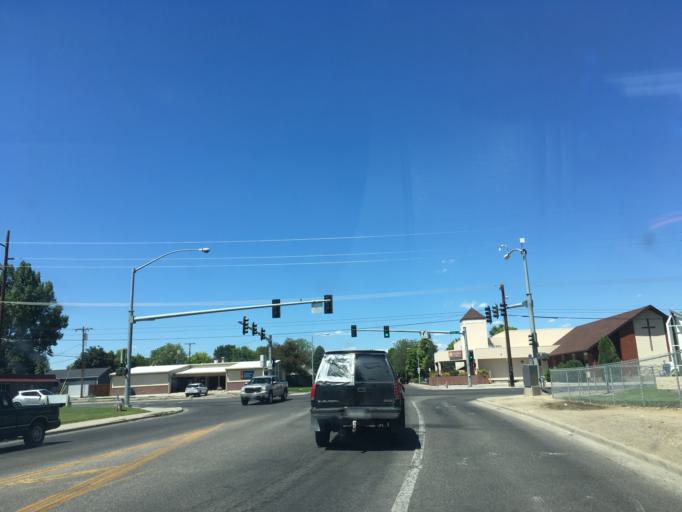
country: US
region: Montana
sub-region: Yellowstone County
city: Billings
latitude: 45.7692
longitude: -108.5647
